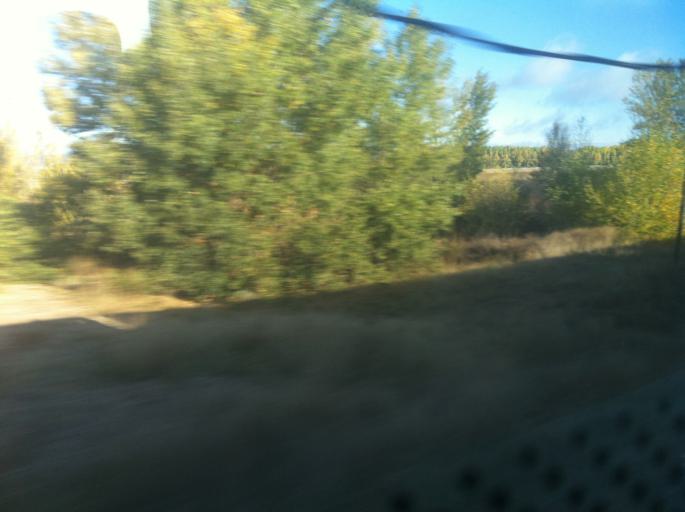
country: ES
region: Castille and Leon
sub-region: Provincia de Palencia
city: Cordovilla la Real
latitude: 42.0346
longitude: -4.2697
